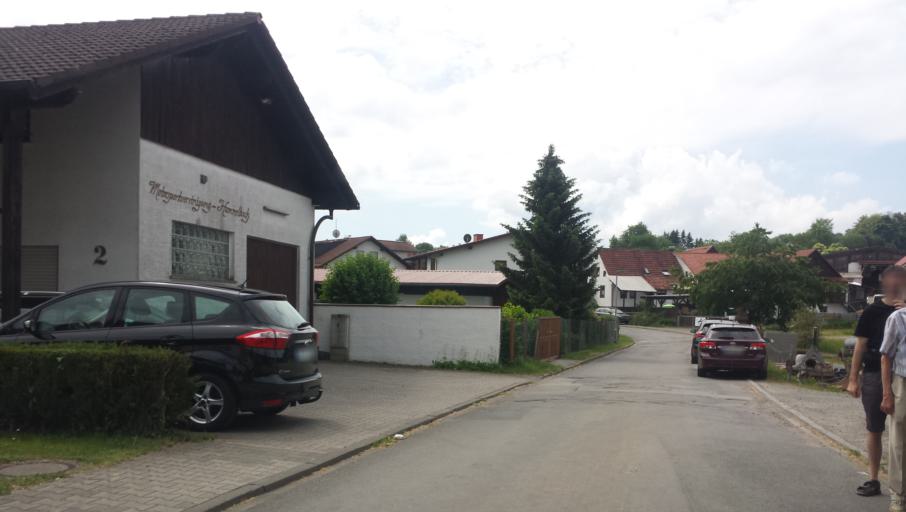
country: DE
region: Hesse
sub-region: Regierungsbezirk Darmstadt
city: Furth
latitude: 49.6349
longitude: 8.8290
